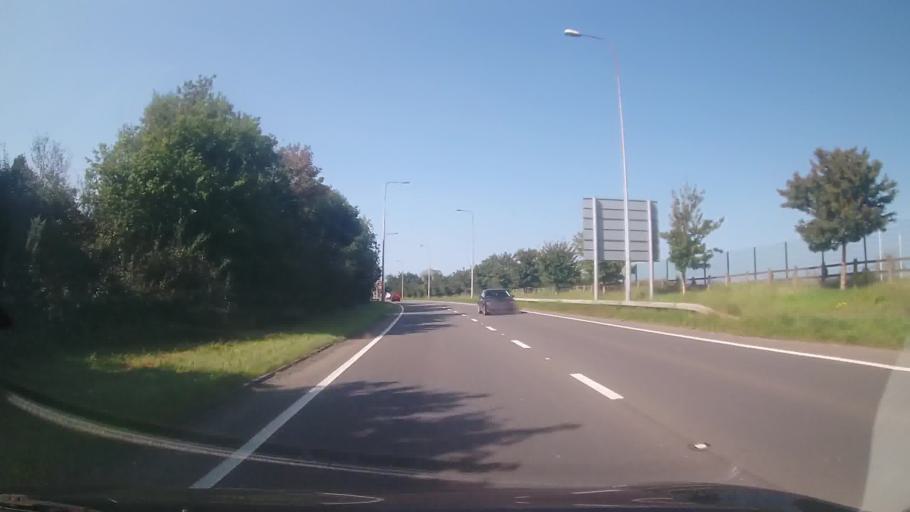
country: GB
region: Wales
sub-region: Pembrokeshire
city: Haverfordwest
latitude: 51.8169
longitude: -4.9581
